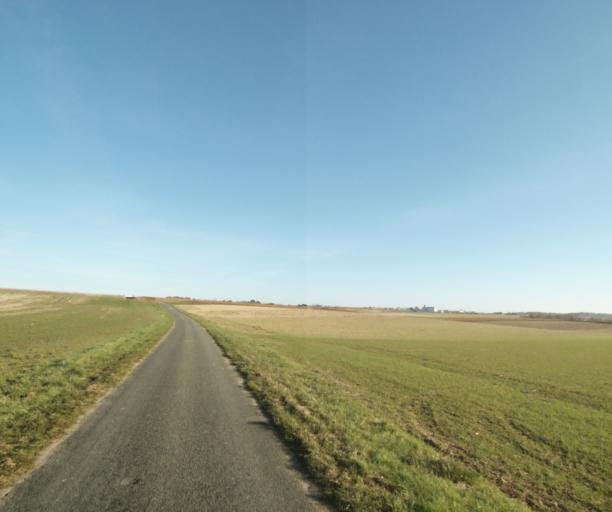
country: FR
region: Poitou-Charentes
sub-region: Departement de la Charente-Maritime
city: Cherac
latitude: 45.6963
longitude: -0.4561
